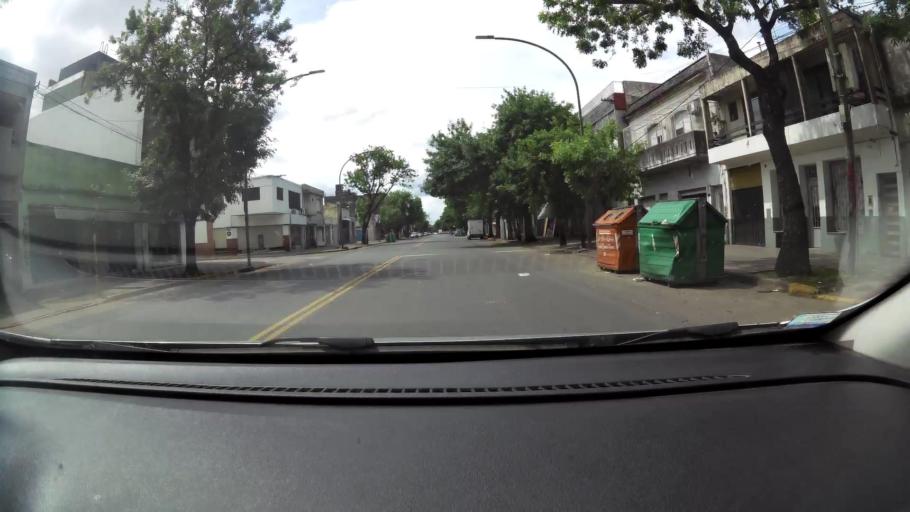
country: AR
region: Santa Fe
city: Gobernador Galvez
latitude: -33.0056
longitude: -60.6359
